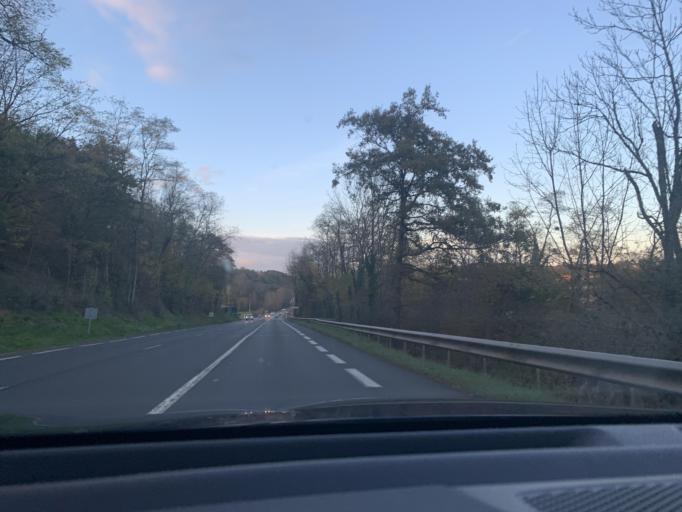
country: FR
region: Rhone-Alpes
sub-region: Departement du Rhone
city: Liergues
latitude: 45.9470
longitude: 4.6615
